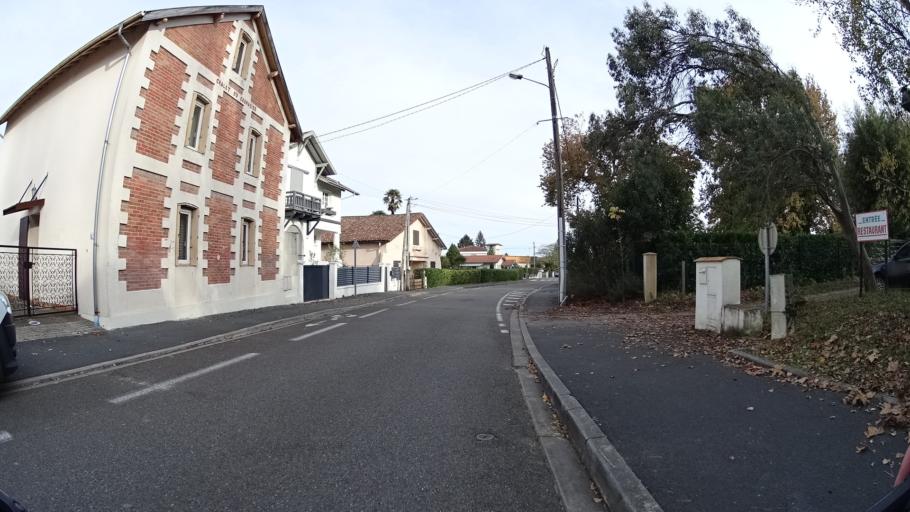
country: FR
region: Aquitaine
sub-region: Departement des Landes
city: Saint-Paul-les-Dax
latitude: 43.7309
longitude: -1.0481
